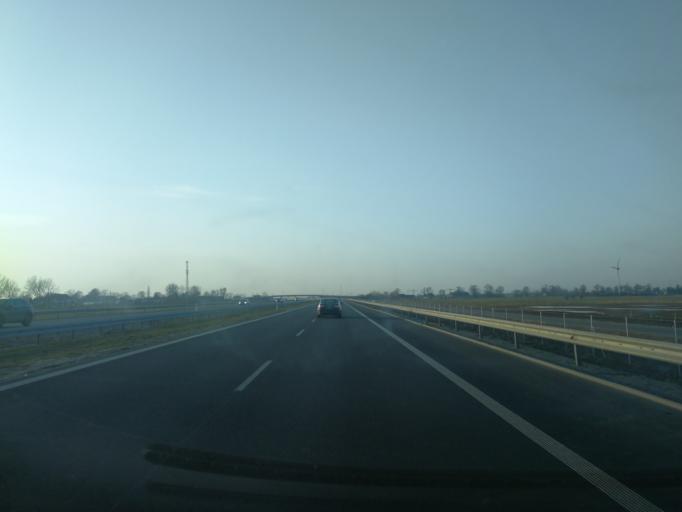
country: PL
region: Pomeranian Voivodeship
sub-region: Powiat nowodworski
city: Ostaszewo
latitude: 54.2471
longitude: 18.9930
